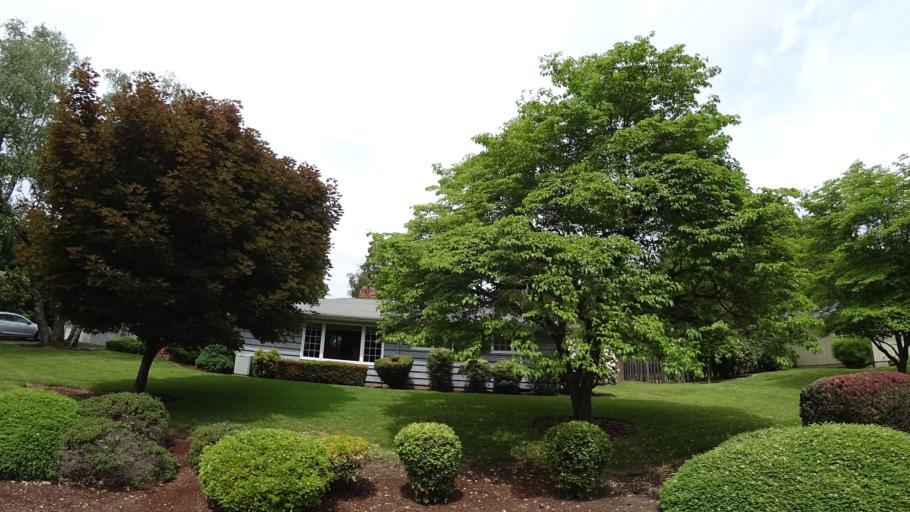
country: US
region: Oregon
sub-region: Washington County
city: Garden Home-Whitford
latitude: 45.4625
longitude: -122.7556
